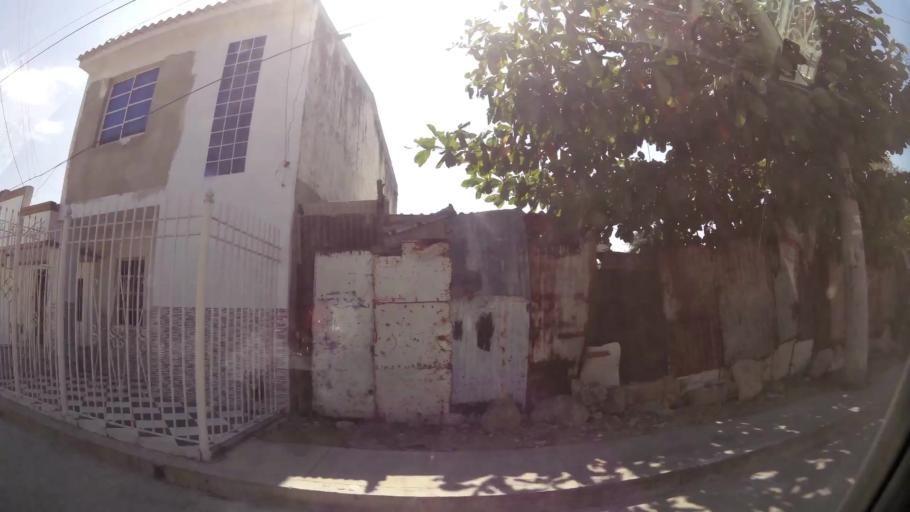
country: CO
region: Atlantico
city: Barranquilla
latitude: 10.9719
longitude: -74.8359
